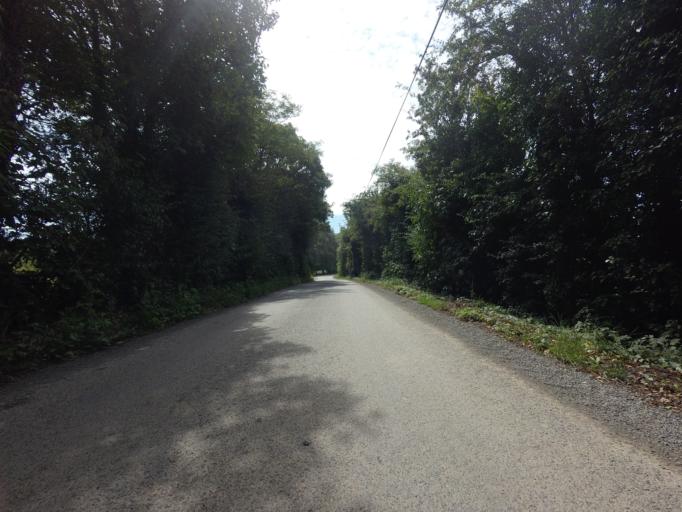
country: GB
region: England
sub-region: Kent
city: Stone
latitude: 50.9945
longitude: 0.8057
